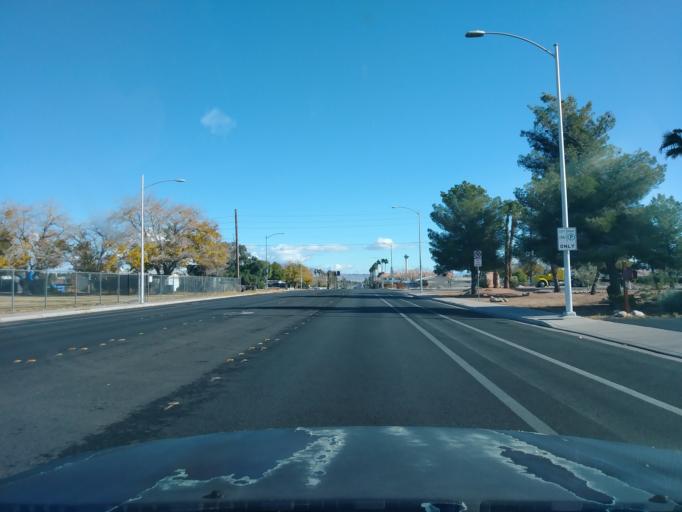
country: US
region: Nevada
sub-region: Clark County
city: Spring Valley
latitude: 36.1517
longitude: -115.2155
